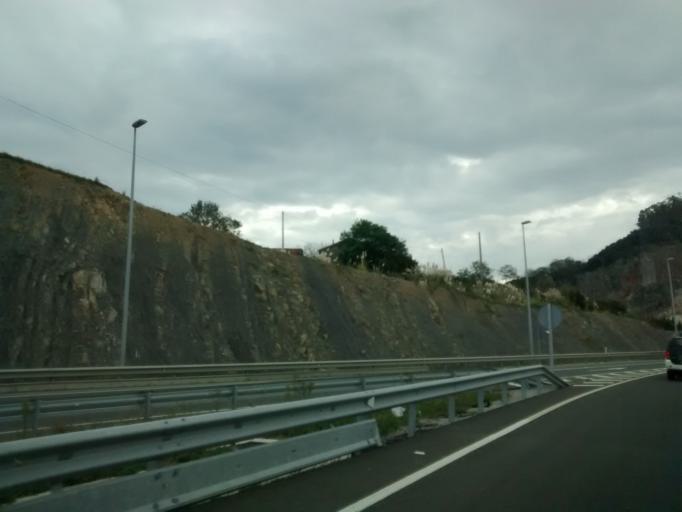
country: ES
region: Cantabria
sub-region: Provincia de Cantabria
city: Lierganes
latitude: 43.3900
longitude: -3.7470
